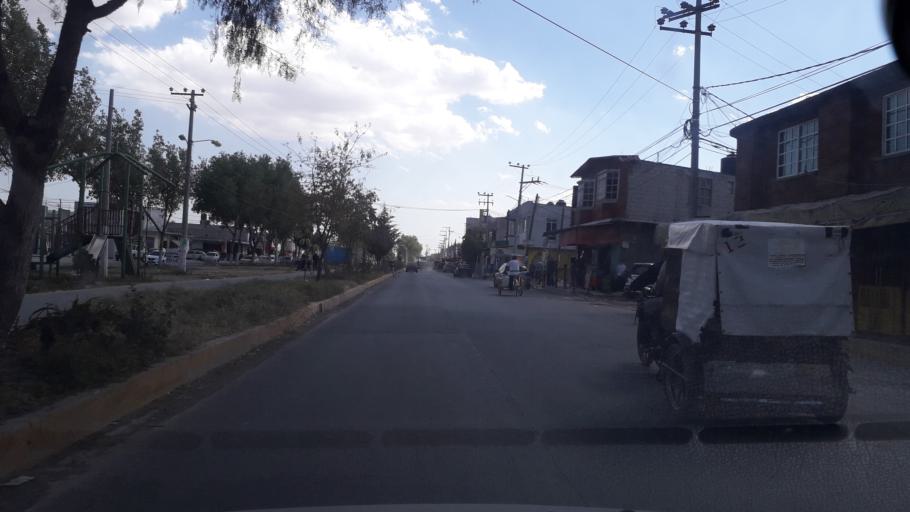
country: MX
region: Mexico
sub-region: Jaltenco
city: Alborada Jaltenco
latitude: 19.6454
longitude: -99.0614
